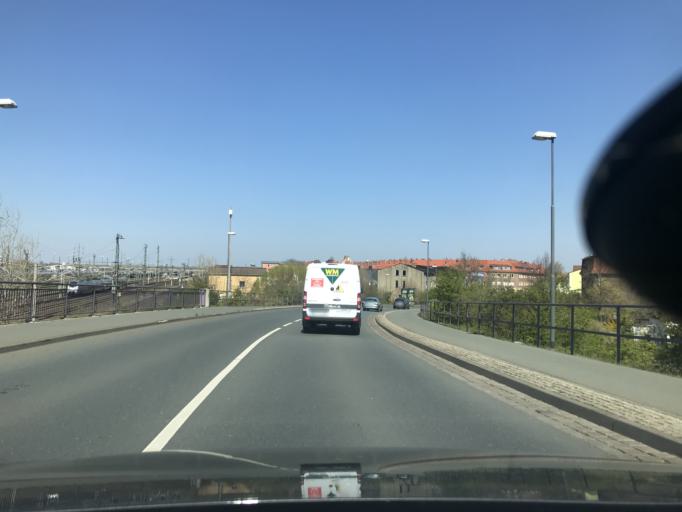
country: DE
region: Saxony
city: Bitterfeld-Wolfen
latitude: 51.6169
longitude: 12.3162
